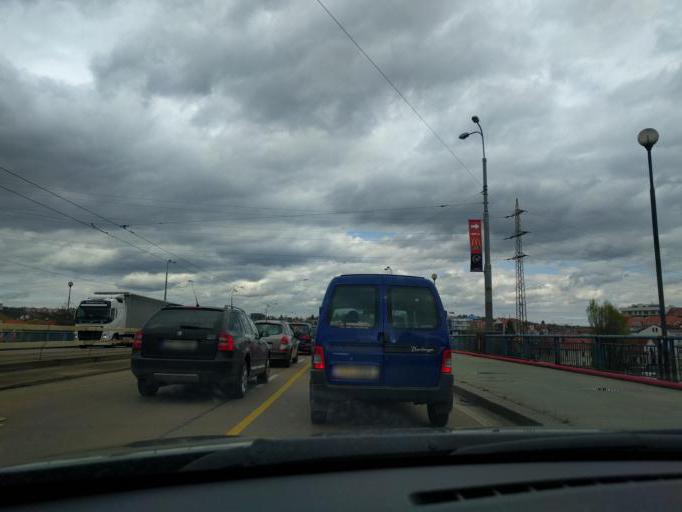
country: CZ
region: Plzensky
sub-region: Okres Plzen-Mesto
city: Pilsen
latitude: 49.7503
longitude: 13.3748
